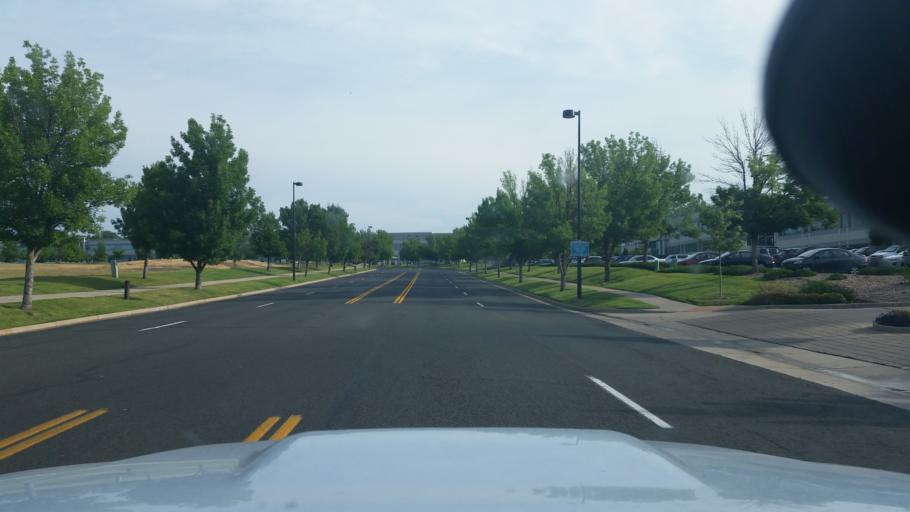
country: US
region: Colorado
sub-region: Broomfield County
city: Broomfield
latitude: 39.8944
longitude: -105.1110
